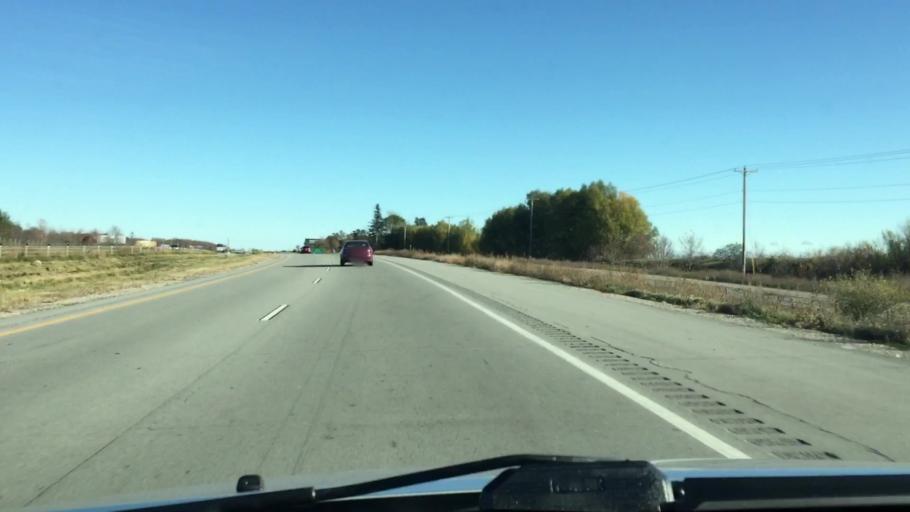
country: US
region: Wisconsin
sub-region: Brown County
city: Wrightstown
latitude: 44.3314
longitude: -88.2078
